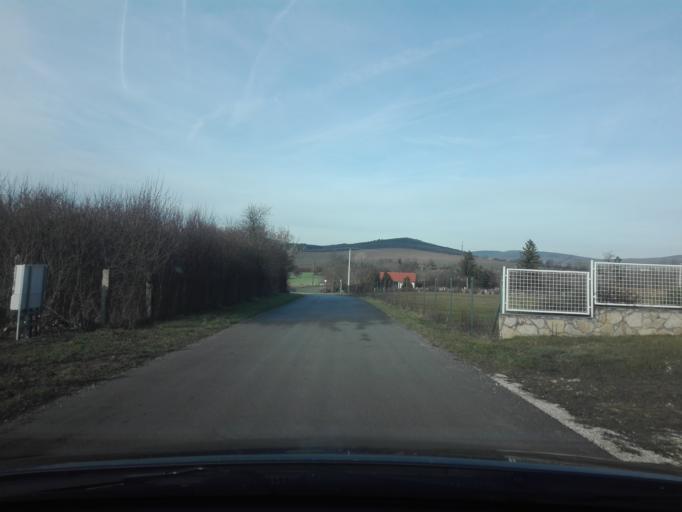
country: HU
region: Veszprem
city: Nemesvamos
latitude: 47.0118
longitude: 17.7875
